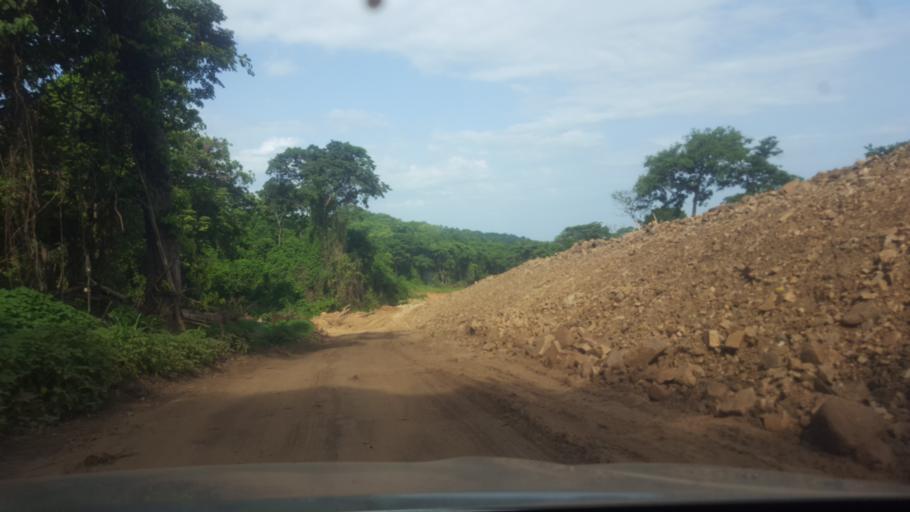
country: ET
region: Southern Nations, Nationalities, and People's Region
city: Tippi
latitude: 7.5395
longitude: 34.9705
